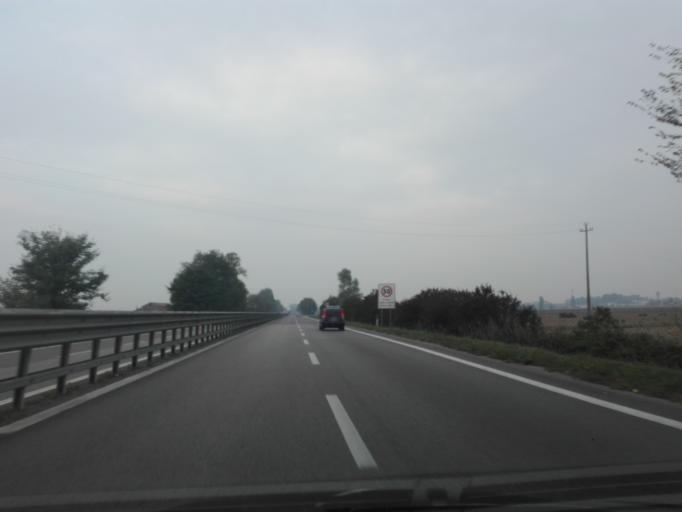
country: IT
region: Veneto
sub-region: Provincia di Rovigo
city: Fratta Polesine
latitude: 45.0212
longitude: 11.6598
